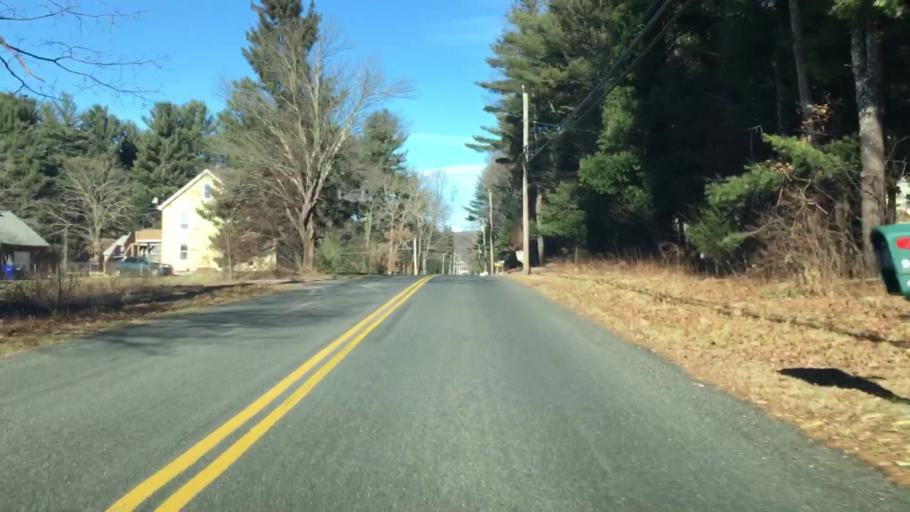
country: US
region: Connecticut
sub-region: Tolland County
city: Crystal Lake
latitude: 41.9235
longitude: -72.3891
